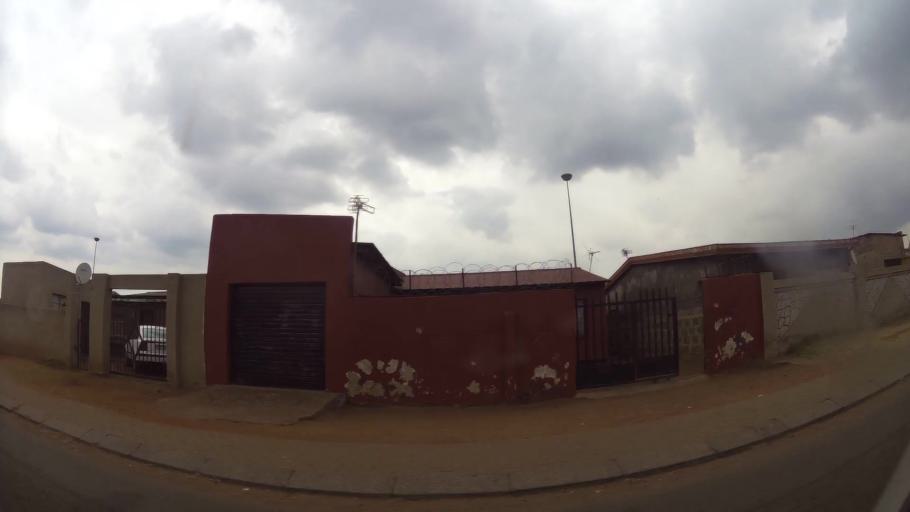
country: ZA
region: Gauteng
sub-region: Ekurhuleni Metropolitan Municipality
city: Germiston
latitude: -26.3561
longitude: 28.1499
